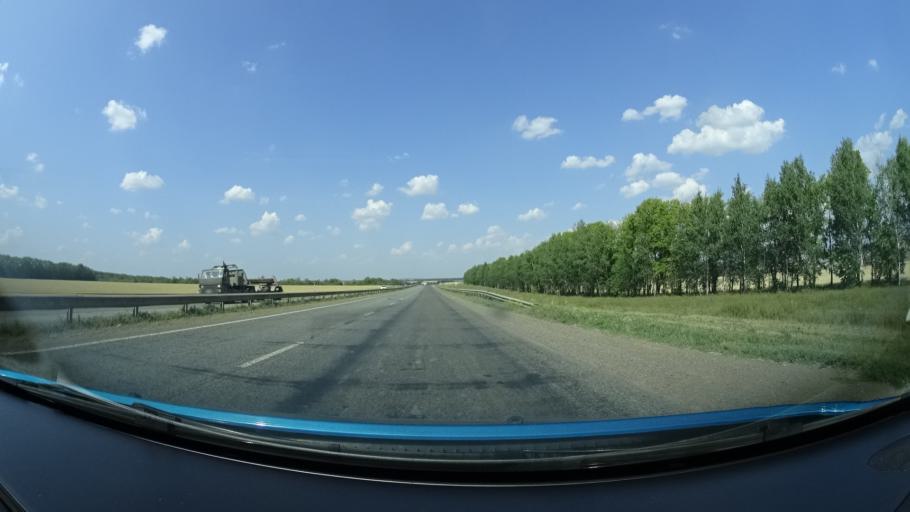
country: RU
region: Bashkortostan
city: Dmitriyevka
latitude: 54.6745
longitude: 55.3622
